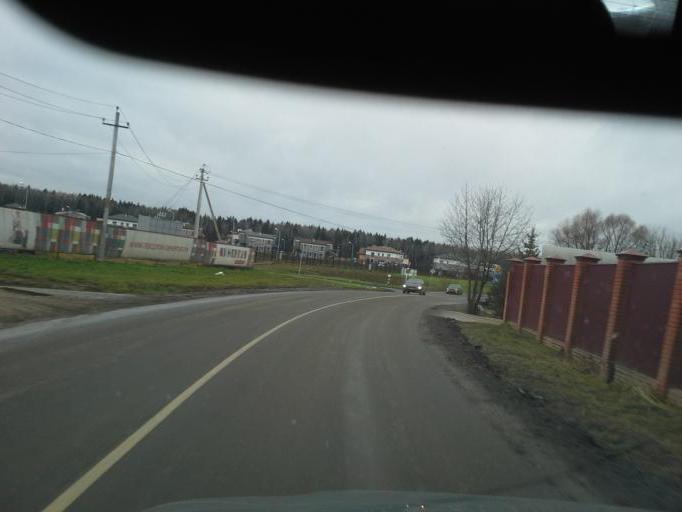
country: RU
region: Moskovskaya
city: Moskovskiy
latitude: 55.5727
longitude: 37.3823
